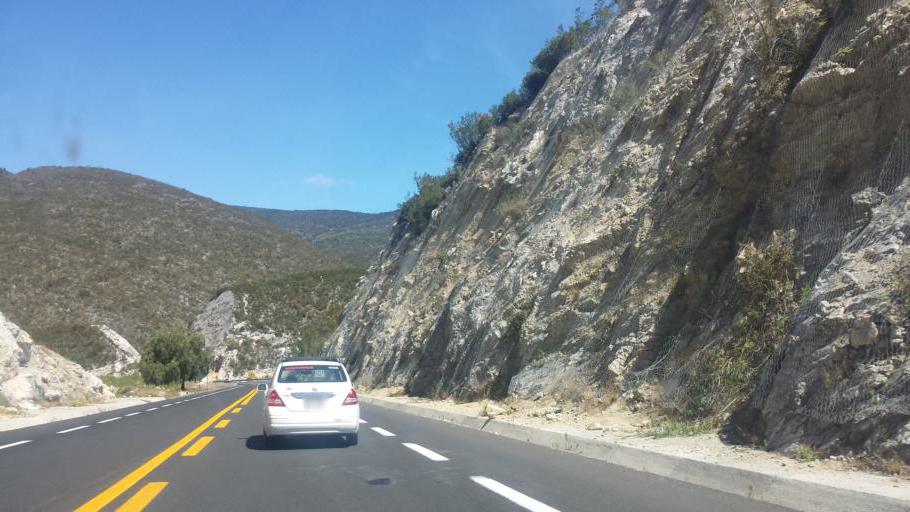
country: MX
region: Puebla
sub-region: San Jose Miahuatlan
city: San Pedro Tetitlan
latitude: 18.0207
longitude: -97.3510
